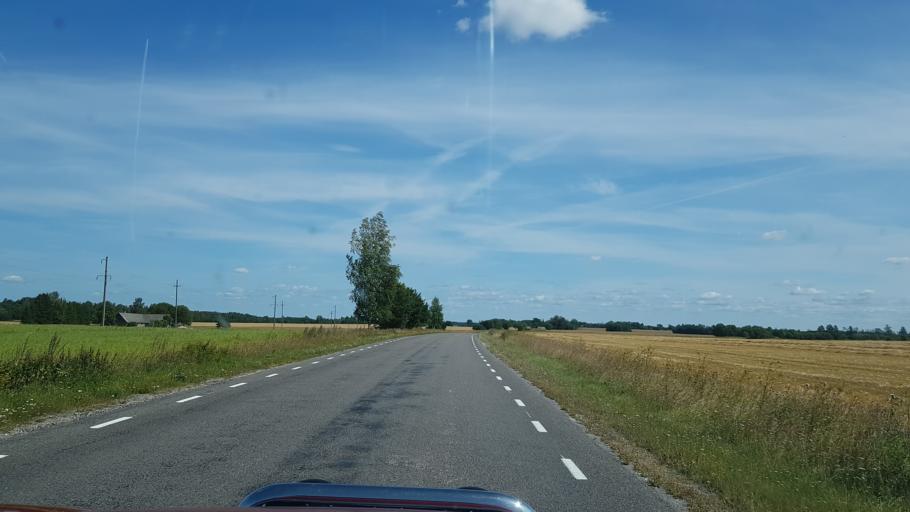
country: EE
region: Jaervamaa
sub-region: Koeru vald
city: Koeru
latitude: 59.0426
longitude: 25.9808
